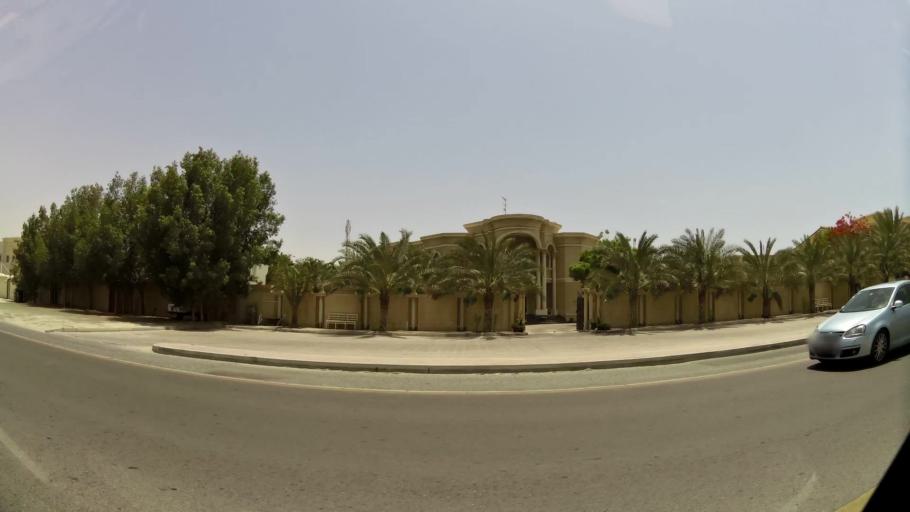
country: AE
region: Dubai
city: Dubai
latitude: 25.1571
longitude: 55.2123
